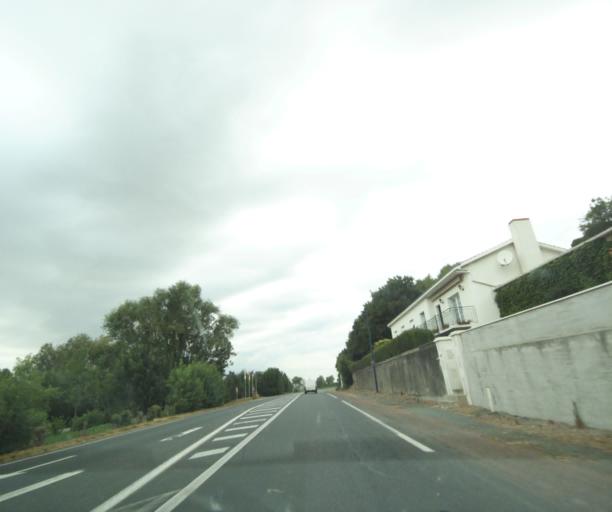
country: FR
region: Pays de la Loire
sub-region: Departement de la Vendee
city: Chaille-les-Marais
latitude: 46.4033
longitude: -1.0346
